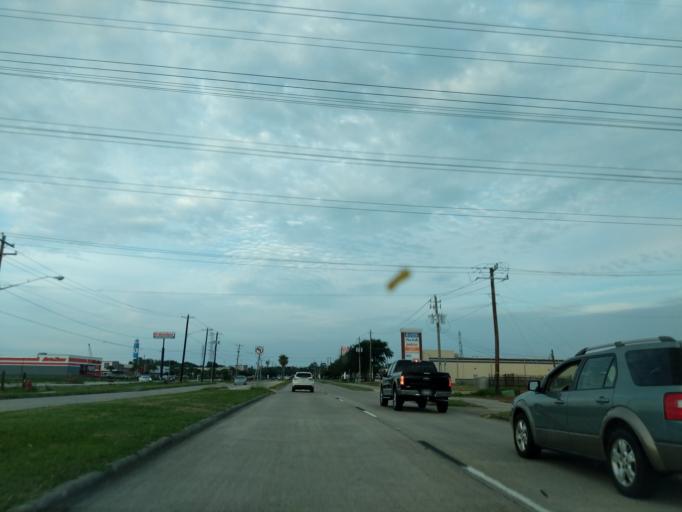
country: US
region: Texas
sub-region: Galveston County
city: Kemah
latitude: 29.5346
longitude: -95.0228
